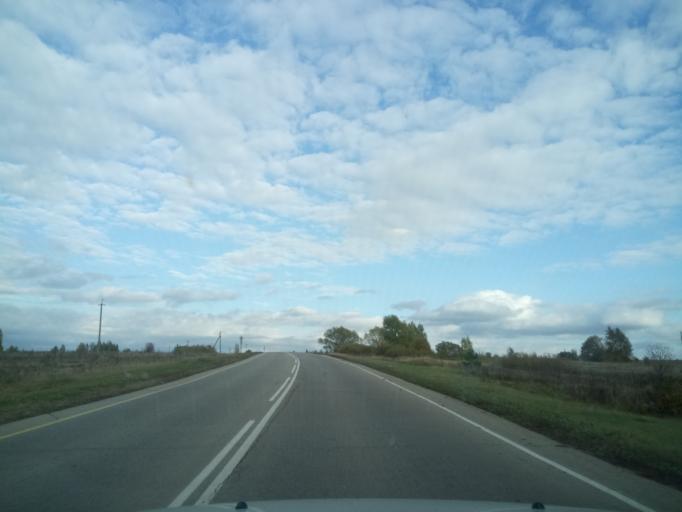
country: RU
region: Nizjnij Novgorod
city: Bol'shoye Boldino
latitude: 54.9645
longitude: 45.2386
